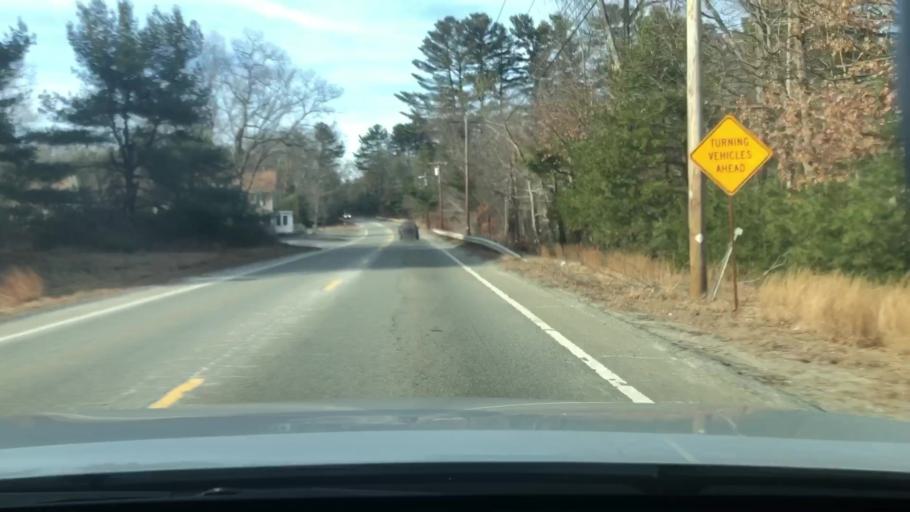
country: US
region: Massachusetts
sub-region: Worcester County
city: Northbridge
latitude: 42.1749
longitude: -71.6326
